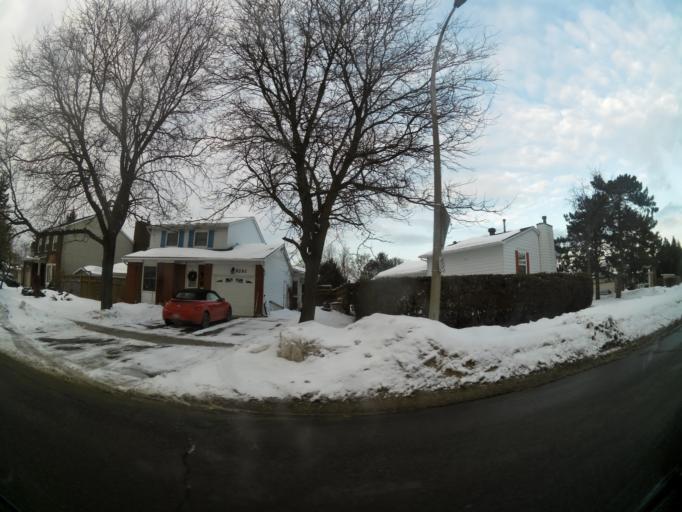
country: CA
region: Quebec
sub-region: Outaouais
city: Gatineau
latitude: 45.4709
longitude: -75.5442
